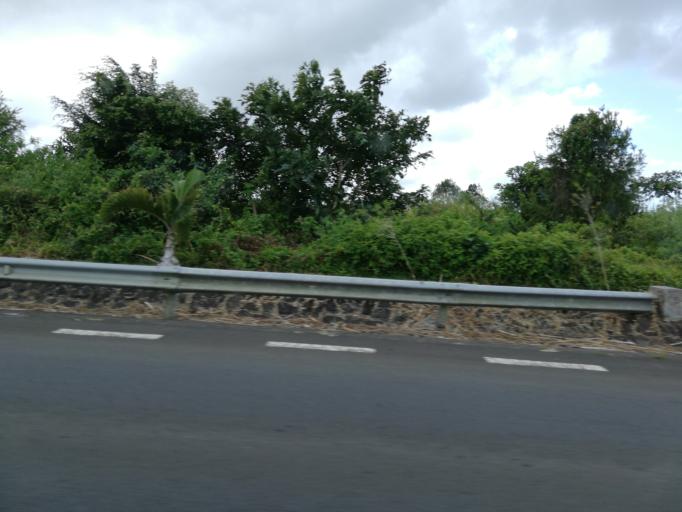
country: MU
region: Grand Port
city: New Grove
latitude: -20.4158
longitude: 57.6042
